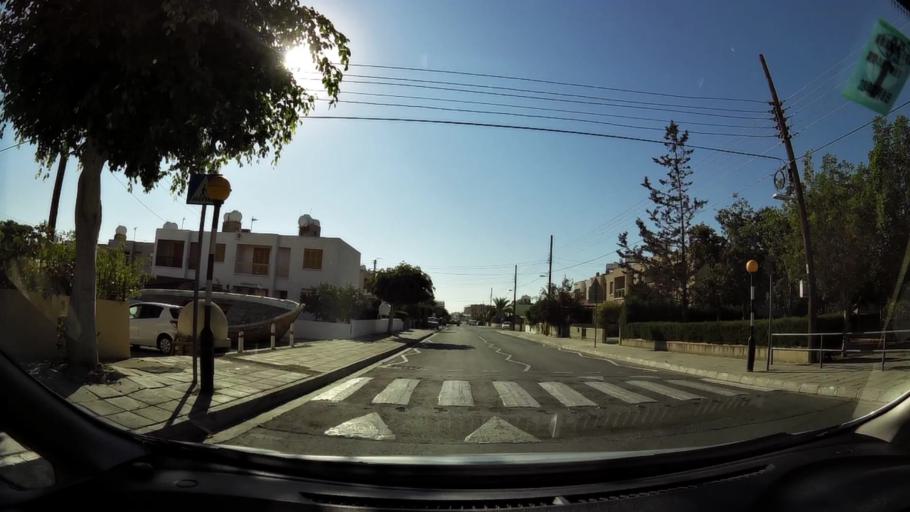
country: CY
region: Larnaka
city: Larnaca
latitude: 34.9356
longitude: 33.6129
